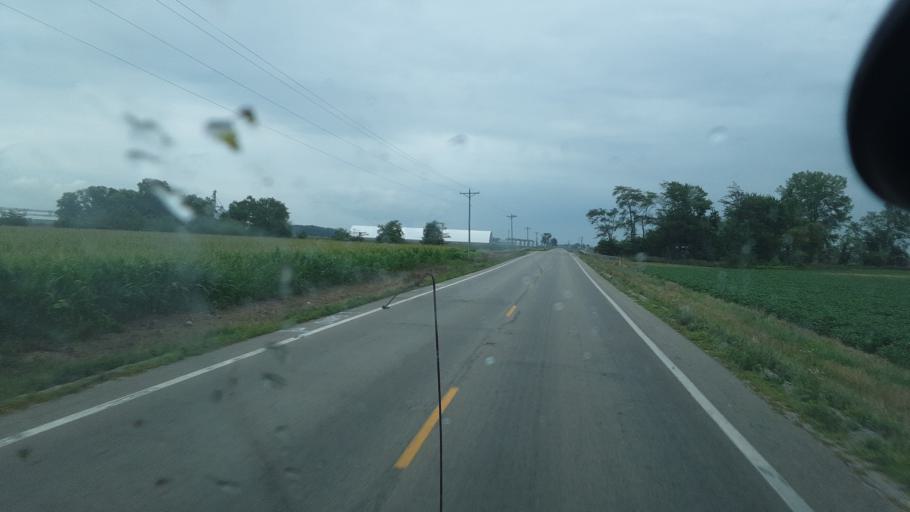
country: US
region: Ohio
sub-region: Defiance County
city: Hicksville
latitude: 41.2960
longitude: -84.7007
